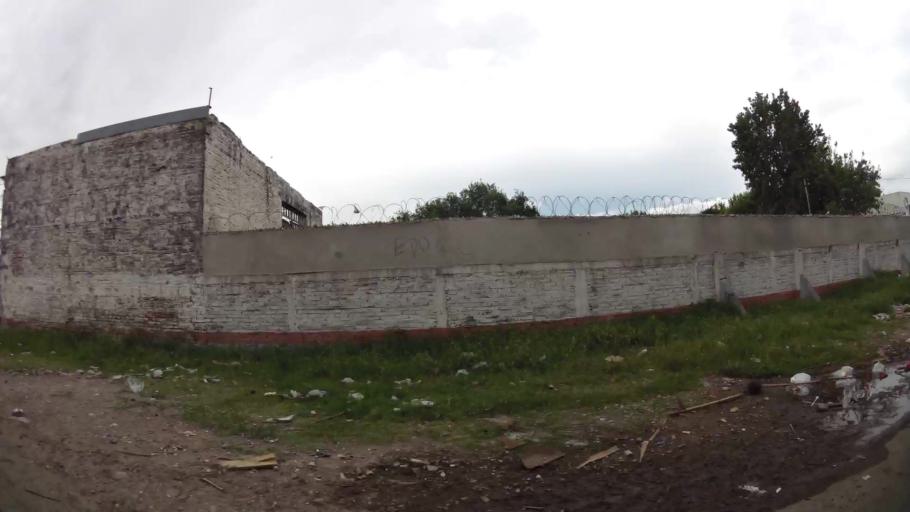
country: AR
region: Santa Fe
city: Gobernador Galvez
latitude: -32.9985
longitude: -60.6734
